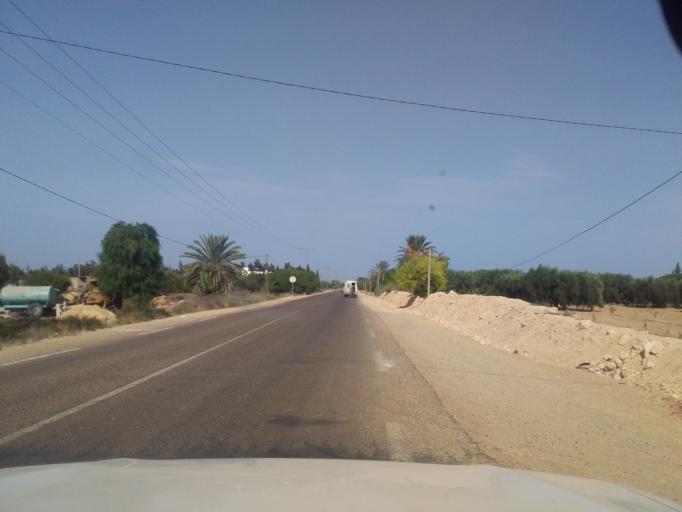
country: TN
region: Qabis
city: Gabes
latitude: 33.6431
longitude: 10.2985
